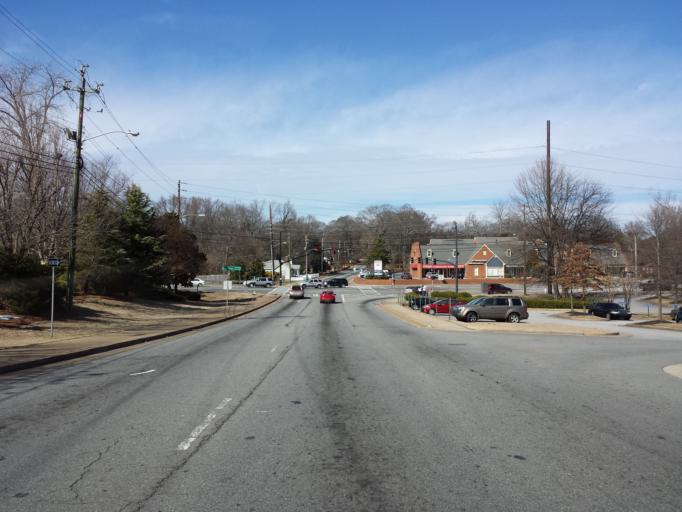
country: US
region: Georgia
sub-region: Cobb County
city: Marietta
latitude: 33.9580
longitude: -84.5491
